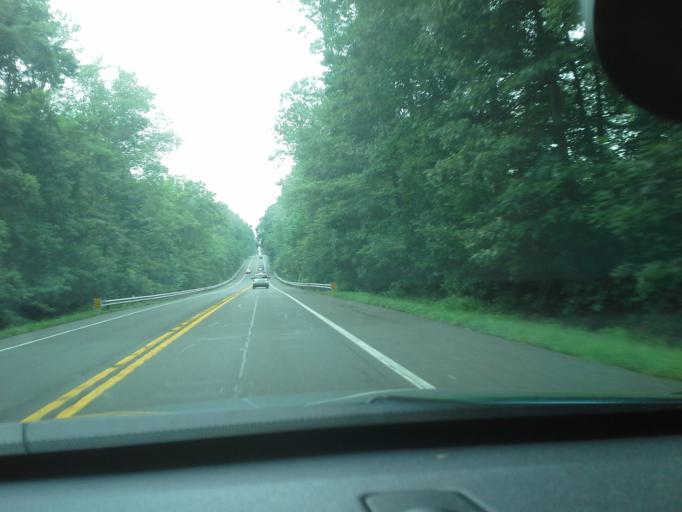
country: US
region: Maryland
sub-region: Calvert County
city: Owings
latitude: 38.7329
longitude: -76.6202
